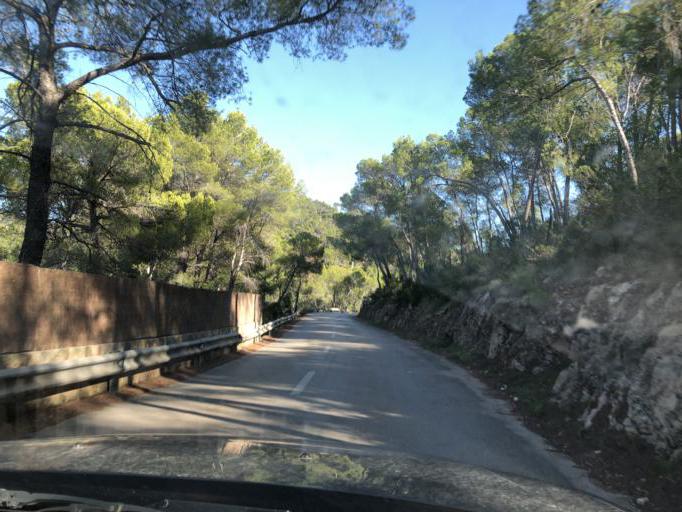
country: ES
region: Balearic Islands
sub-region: Illes Balears
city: Camp de Mar
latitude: 39.5426
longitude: 2.4000
